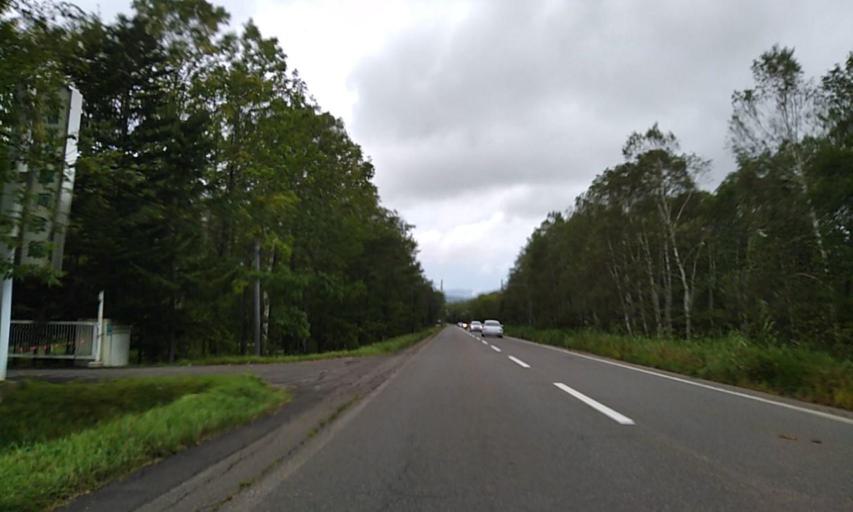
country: JP
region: Hokkaido
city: Bihoro
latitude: 43.5174
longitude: 144.4259
